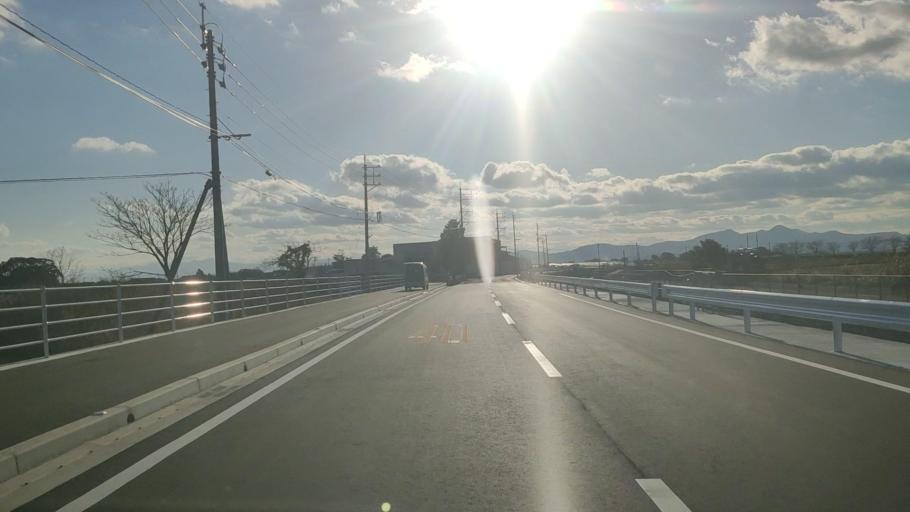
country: JP
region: Saga Prefecture
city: Saga-shi
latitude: 33.3030
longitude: 130.2542
